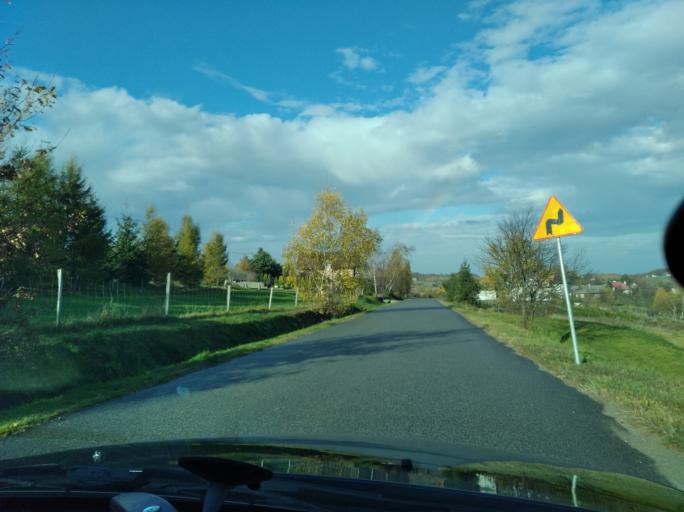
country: PL
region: Subcarpathian Voivodeship
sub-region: Powiat ropczycko-sedziszowski
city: Niedzwiada
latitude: 50.0137
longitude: 21.4795
